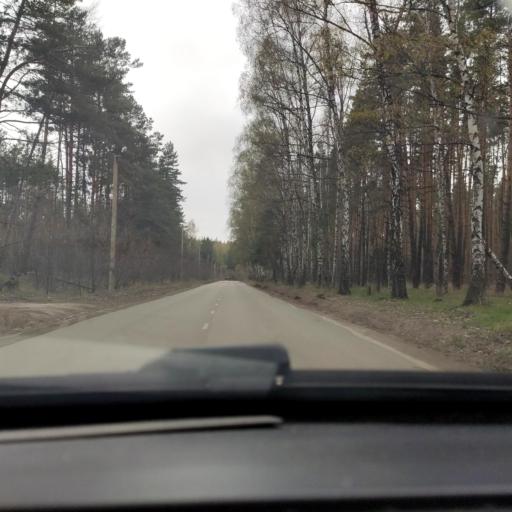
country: RU
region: Voronezj
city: Podgornoye
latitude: 51.7488
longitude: 39.1589
